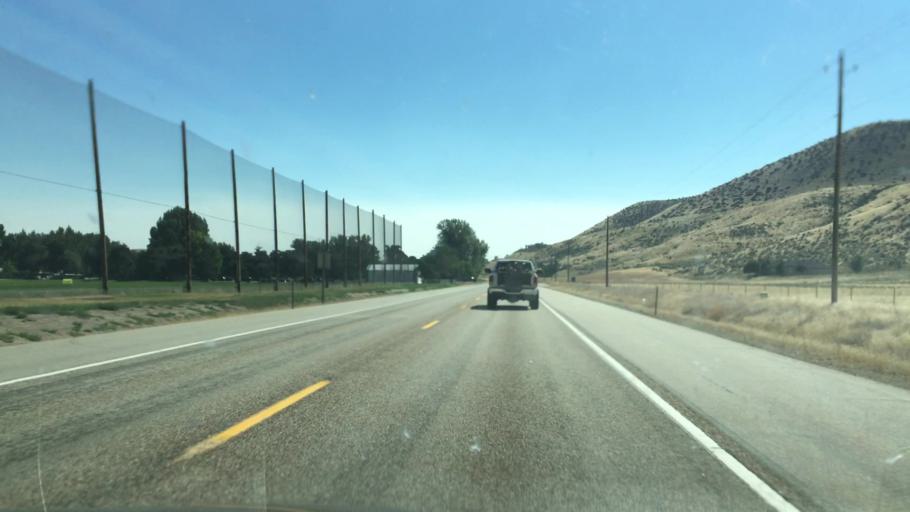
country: US
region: Idaho
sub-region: Ada County
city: Eagle
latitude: 43.7486
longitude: -116.2932
